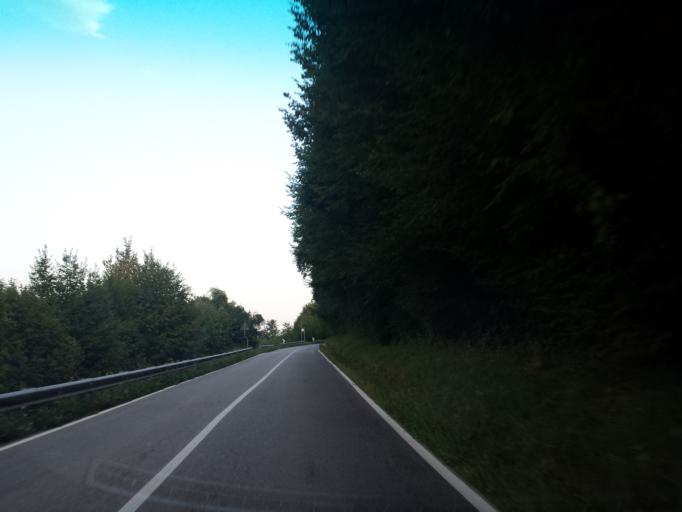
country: IT
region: Veneto
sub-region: Provincia di Vicenza
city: Cogollo del Cengio
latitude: 45.7808
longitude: 11.3988
